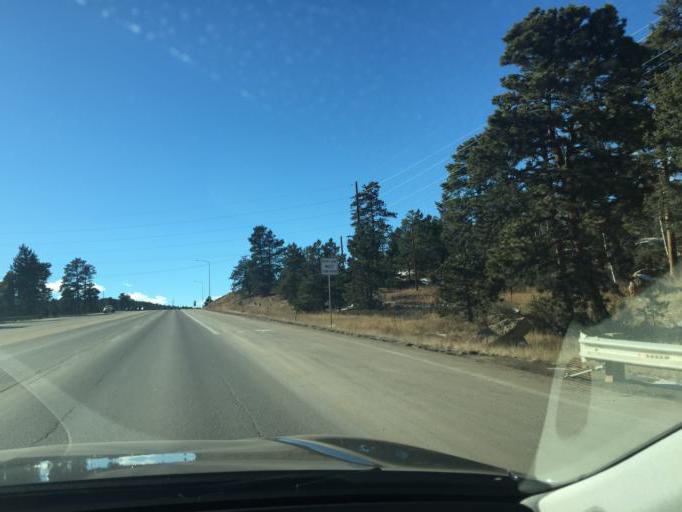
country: US
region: Colorado
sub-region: Jefferson County
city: Evergreen
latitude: 39.5036
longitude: -105.3191
